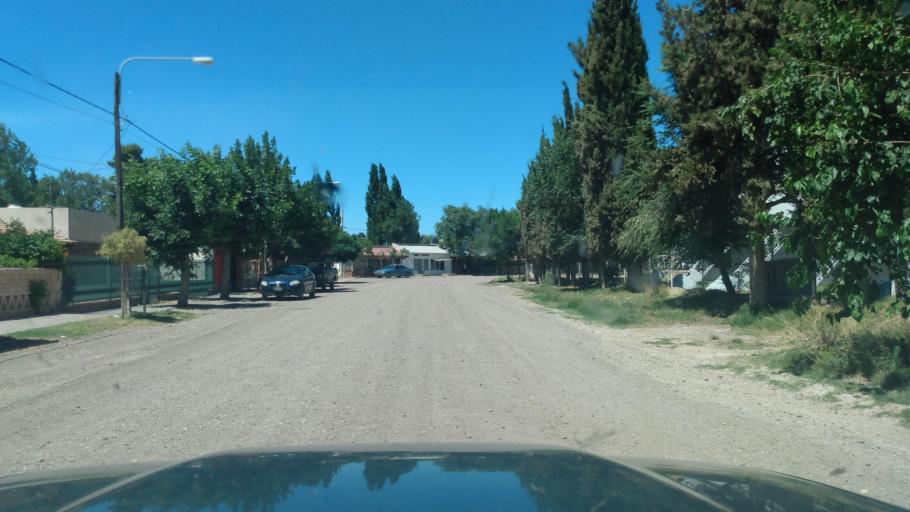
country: AR
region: Neuquen
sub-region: Departamento de Picun Leufu
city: Picun Leufu
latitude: -39.5184
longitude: -69.2890
